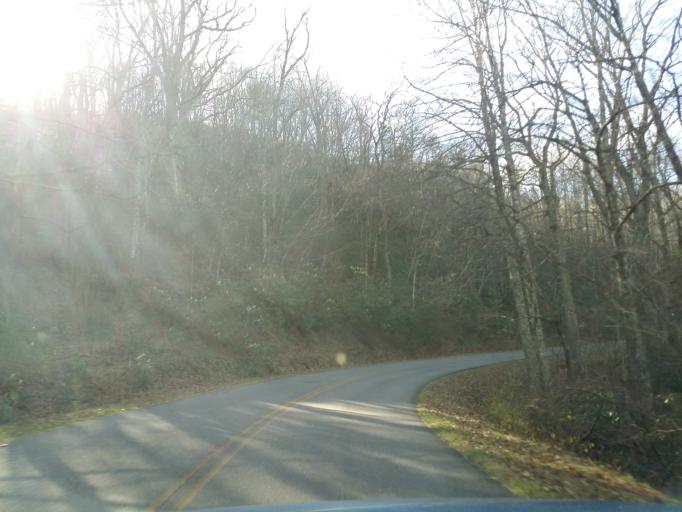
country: US
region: North Carolina
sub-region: McDowell County
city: West Marion
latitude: 35.7552
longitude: -82.1808
